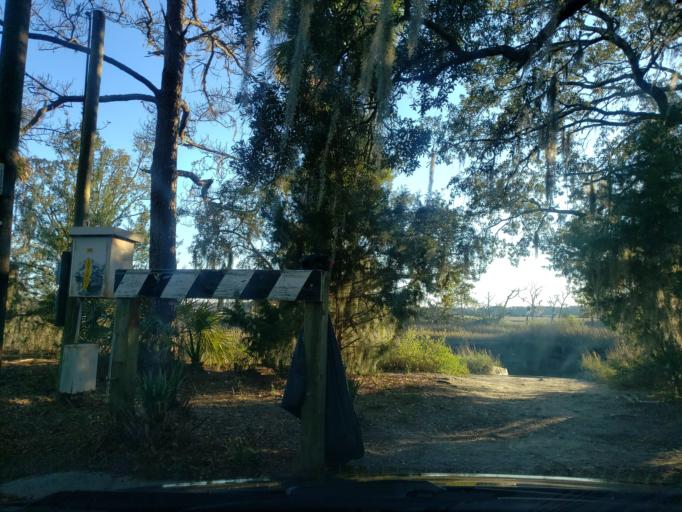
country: US
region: Georgia
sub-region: Chatham County
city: Montgomery
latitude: 31.9869
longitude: -81.1162
